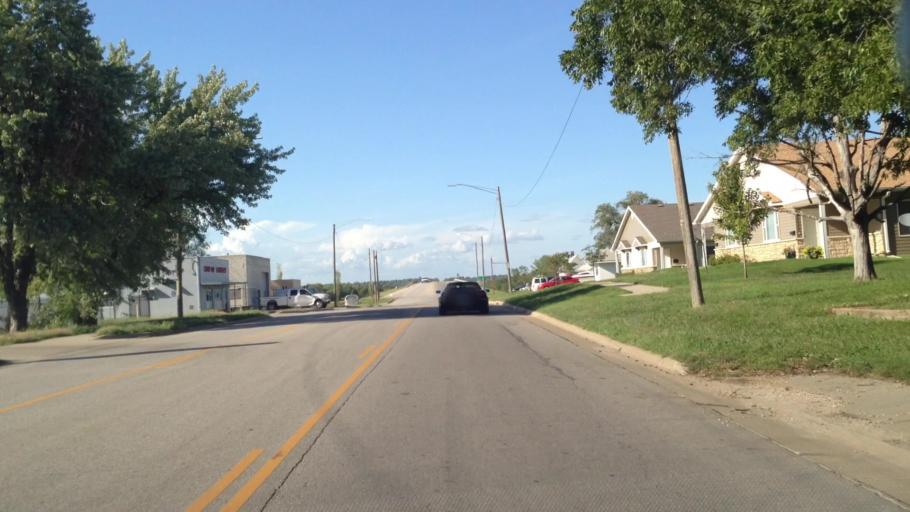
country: US
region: Kansas
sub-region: Franklin County
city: Ottawa
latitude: 38.6321
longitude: -95.2677
